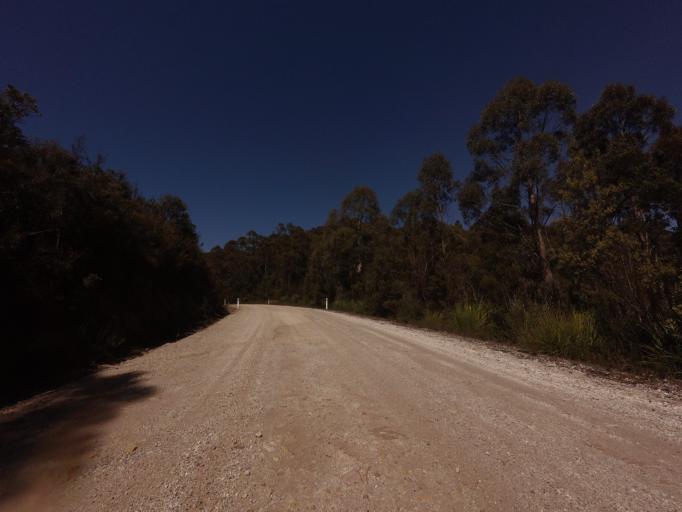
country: AU
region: Tasmania
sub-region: Huon Valley
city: Geeveston
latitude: -42.9839
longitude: 146.3638
